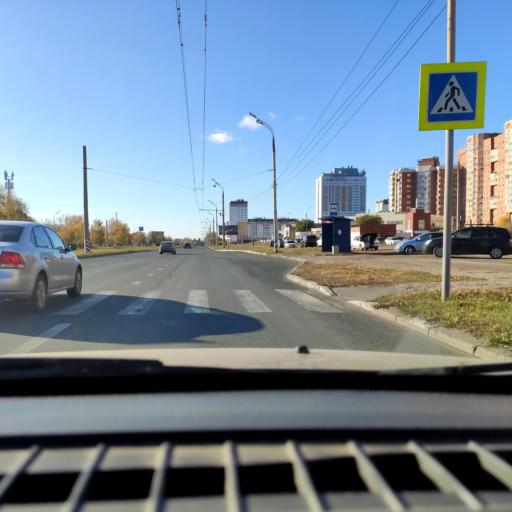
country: RU
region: Samara
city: Tol'yatti
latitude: 53.4993
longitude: 49.2802
